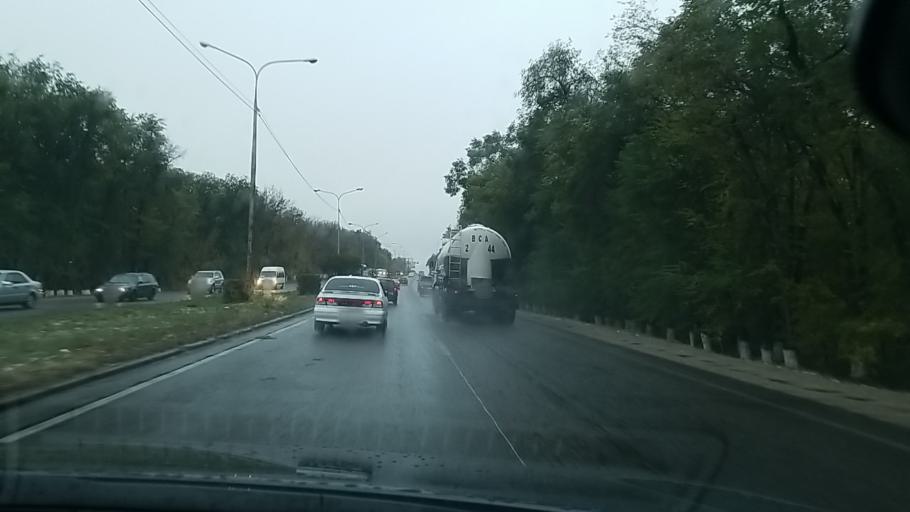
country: KZ
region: Almaty Oblysy
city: Burunday
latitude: 43.2148
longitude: 76.6913
